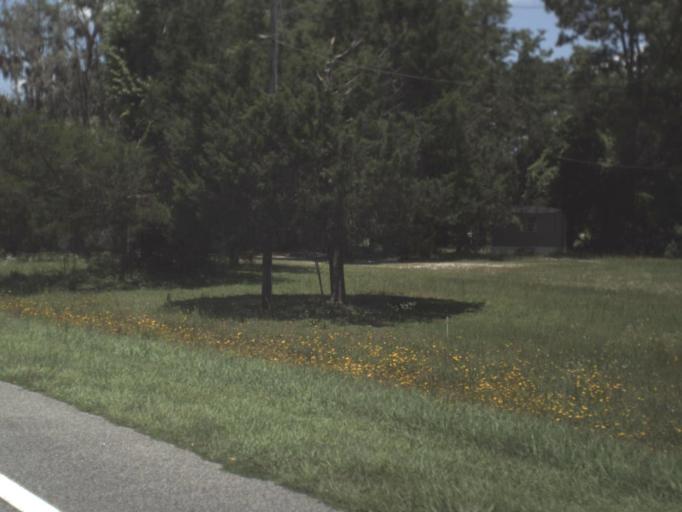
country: US
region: Florida
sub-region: Alachua County
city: High Springs
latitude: 29.9366
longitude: -82.7341
